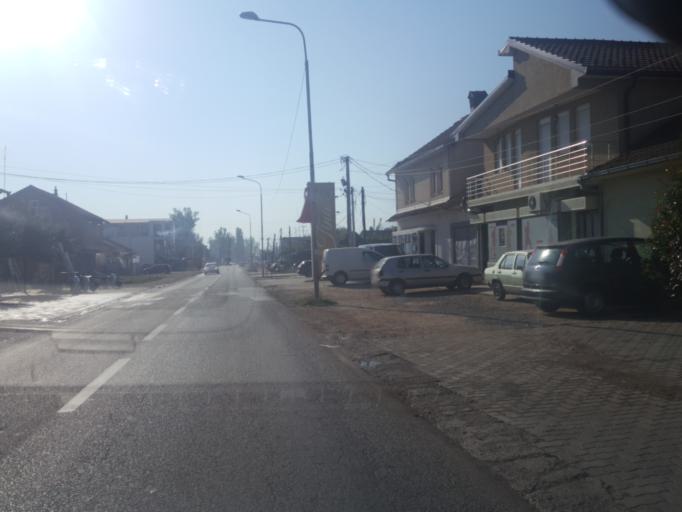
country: XK
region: Gjakova
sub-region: Komuna e Gjakoves
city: Gjakove
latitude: 42.4004
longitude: 20.4158
